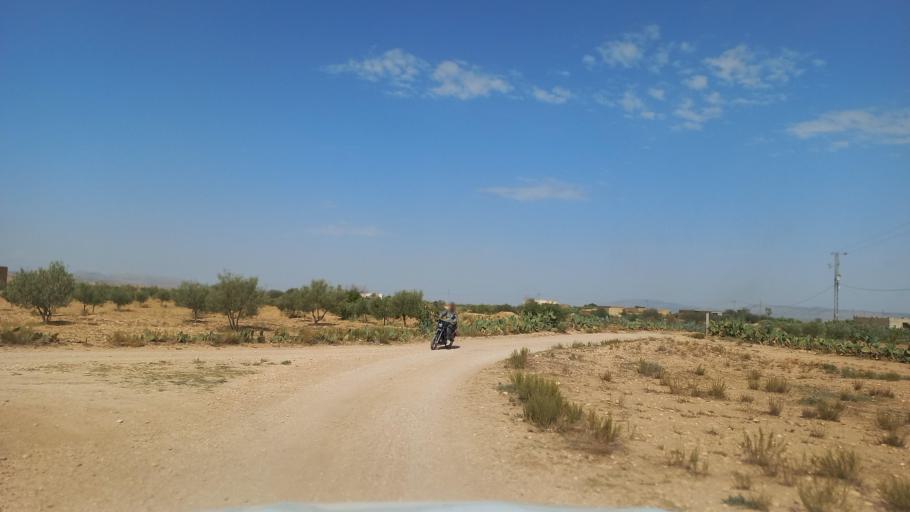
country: TN
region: Al Qasrayn
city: Kasserine
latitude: 35.2790
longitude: 8.9545
